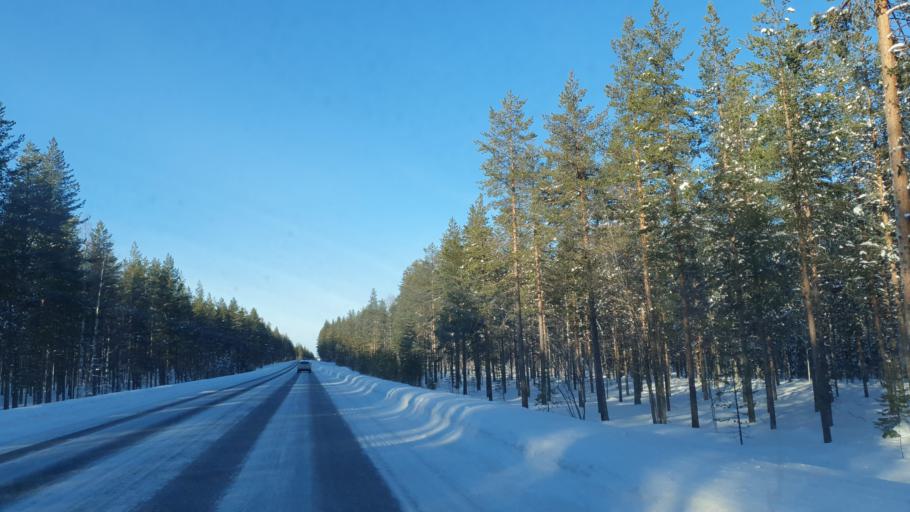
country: FI
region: Lapland
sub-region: Torniolaakso
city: Pello
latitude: 66.9610
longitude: 24.0562
